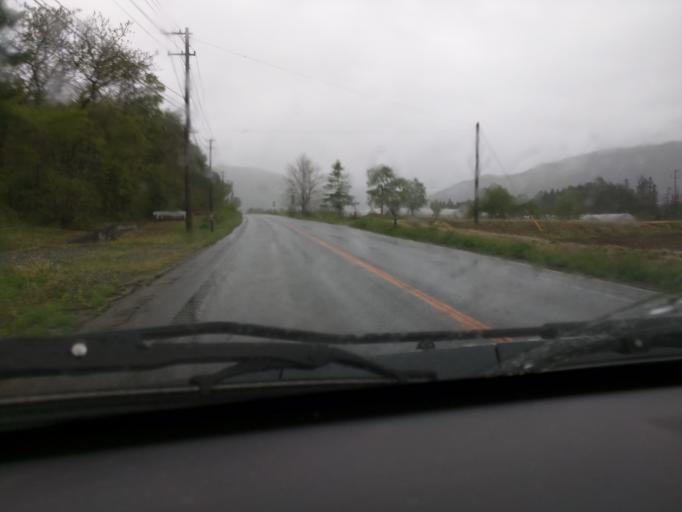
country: JP
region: Fukushima
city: Inawashiro
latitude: 37.5854
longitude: 140.1246
